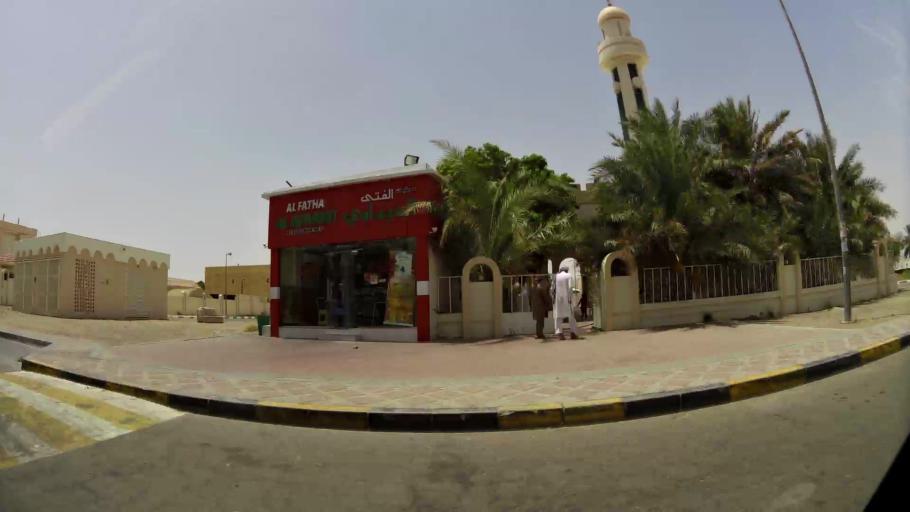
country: AE
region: Abu Dhabi
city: Al Ain
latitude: 24.1925
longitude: 55.7309
